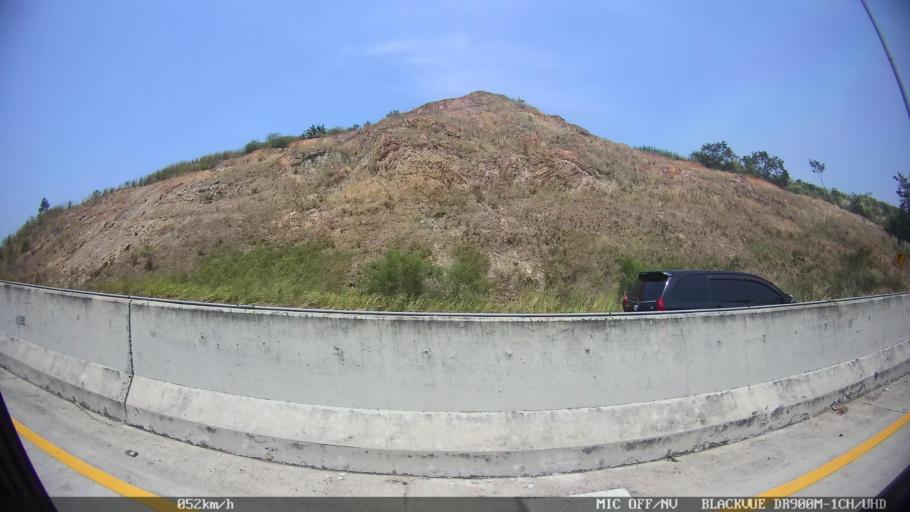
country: ID
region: Lampung
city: Panjang
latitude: -5.4035
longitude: 105.3460
